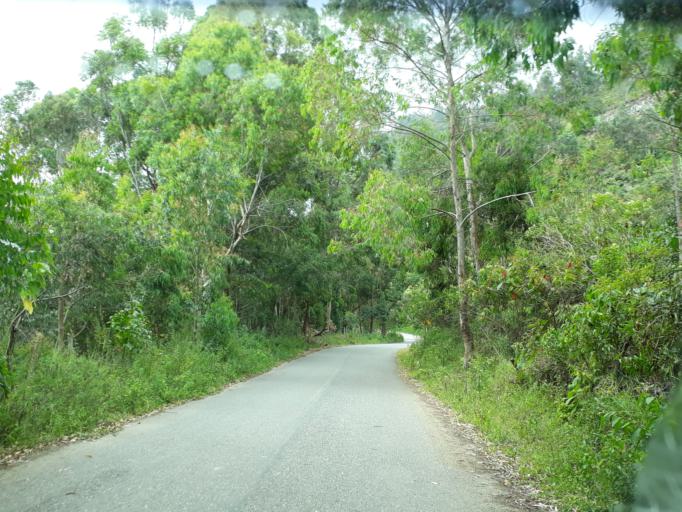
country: CO
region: Cundinamarca
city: Cabrera
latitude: 4.0182
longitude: -74.5116
